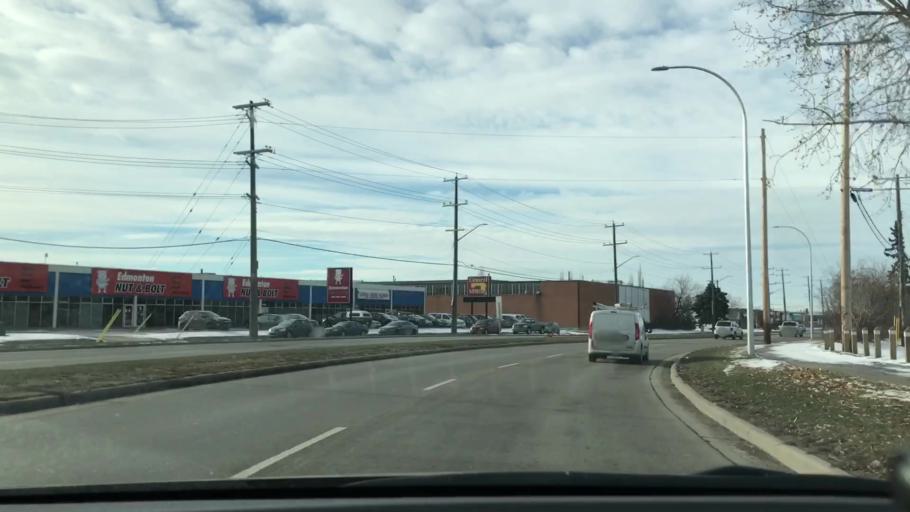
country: CA
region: Alberta
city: Edmonton
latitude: 53.5001
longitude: -113.4594
